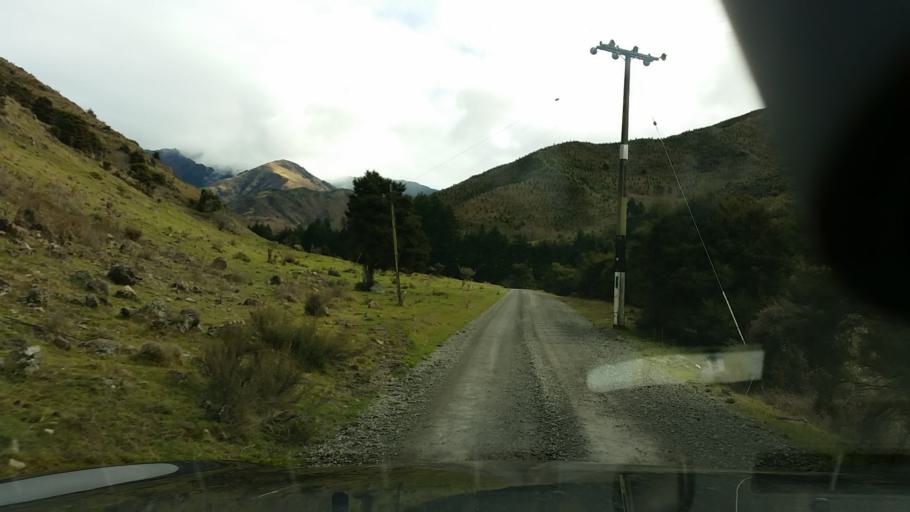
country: NZ
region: Tasman
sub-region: Tasman District
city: Richmond
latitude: -41.7318
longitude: 173.4584
